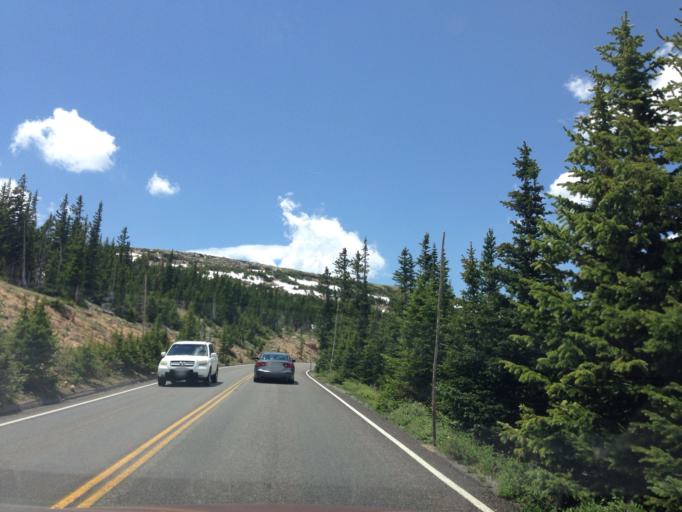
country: US
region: Colorado
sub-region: Larimer County
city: Estes Park
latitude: 40.3933
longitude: -105.6849
